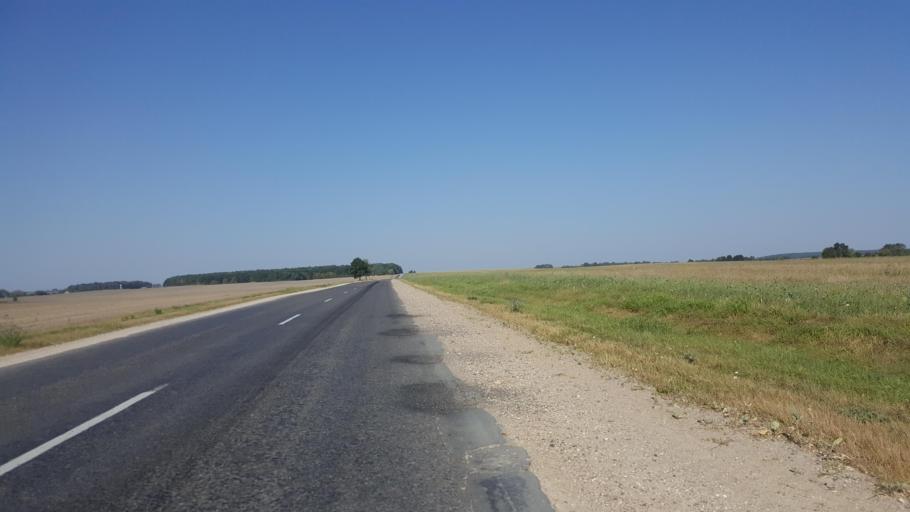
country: BY
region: Brest
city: Kamyanyets
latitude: 52.4099
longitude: 23.7274
